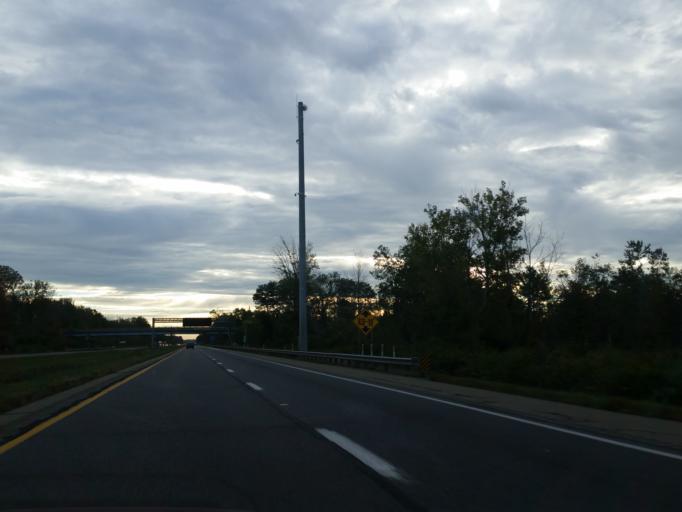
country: US
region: Ohio
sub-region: Ashtabula County
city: Conneaut
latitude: 41.9432
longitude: -80.5039
